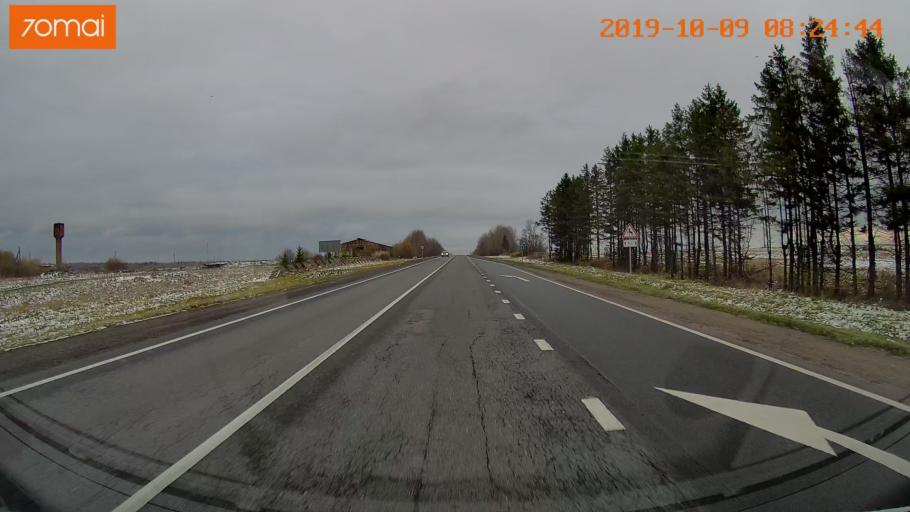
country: RU
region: Vologda
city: Gryazovets
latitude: 58.7707
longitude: 40.2766
